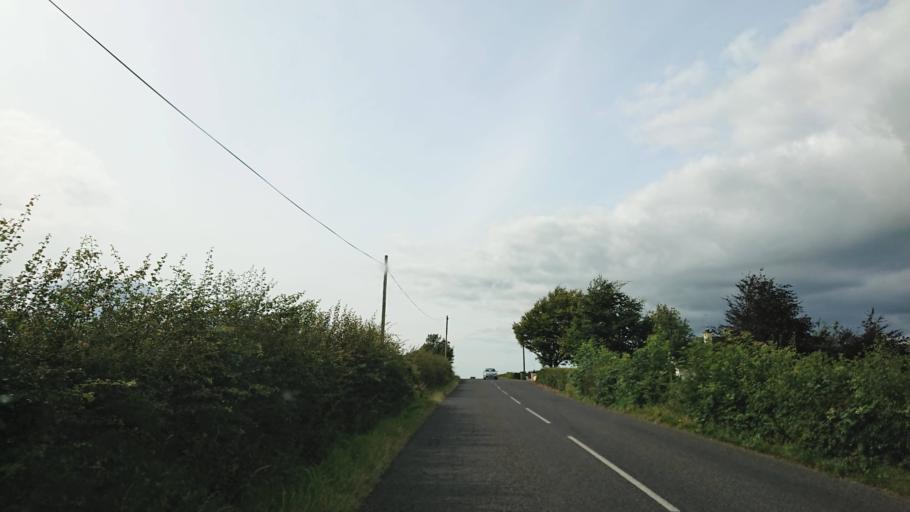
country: GB
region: Northern Ireland
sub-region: Fermanagh District
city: Enniskillen
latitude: 54.2868
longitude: -7.8650
